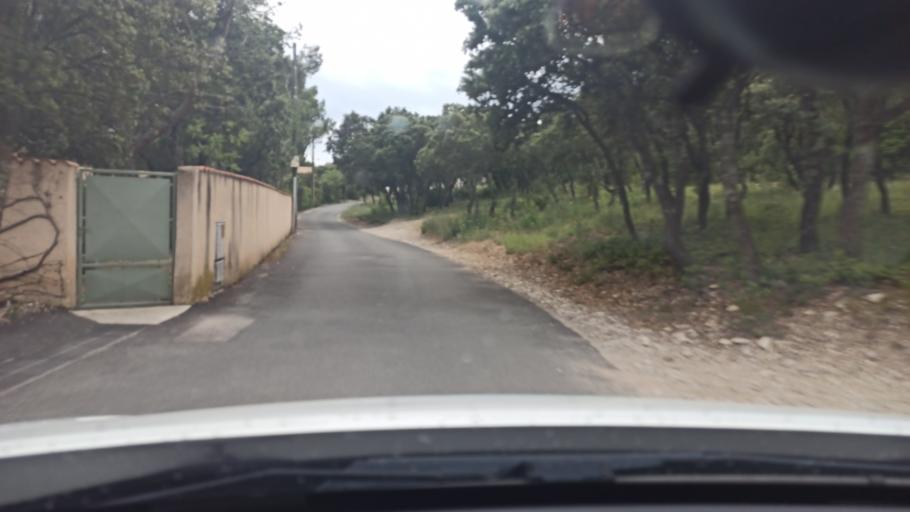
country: FR
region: Languedoc-Roussillon
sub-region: Departement du Gard
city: Les Angles
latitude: 43.9714
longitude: 4.7670
